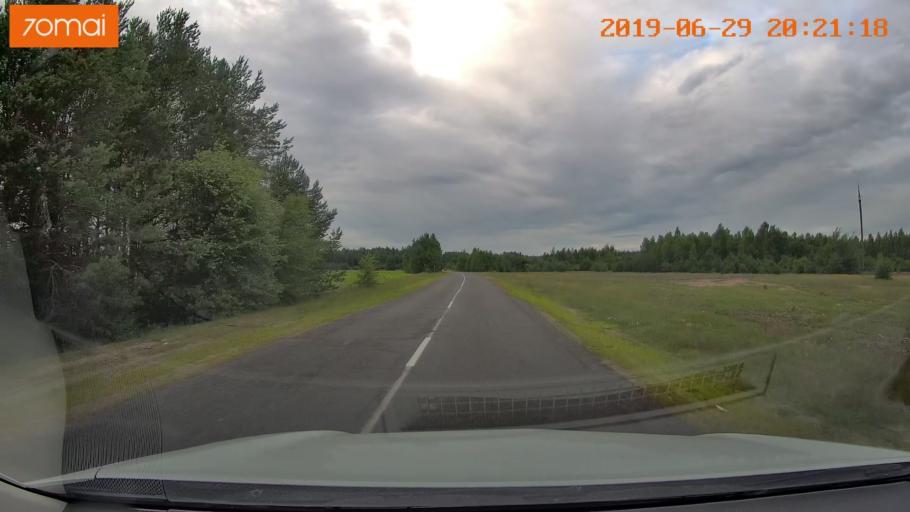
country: BY
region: Brest
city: Asnyezhytsy
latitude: 52.4184
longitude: 26.2527
